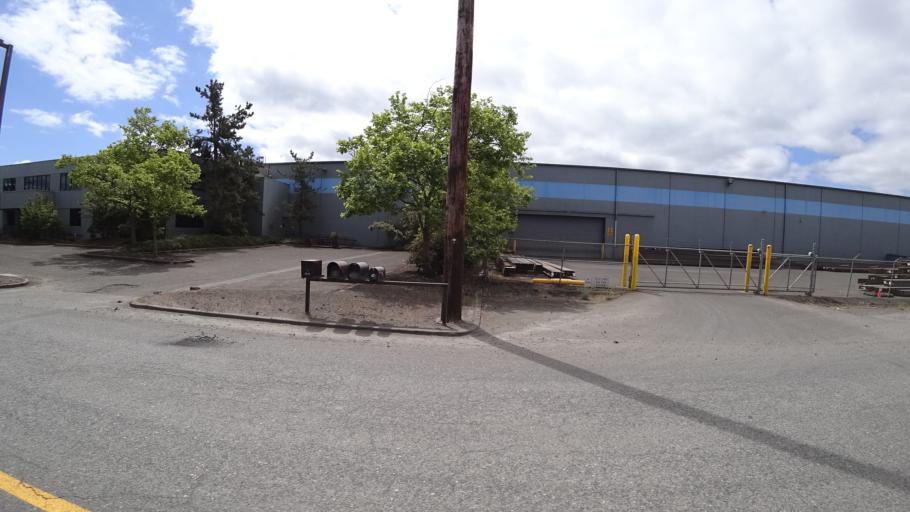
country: US
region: Oregon
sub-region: Washington County
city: West Haven
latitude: 45.6126
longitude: -122.7705
